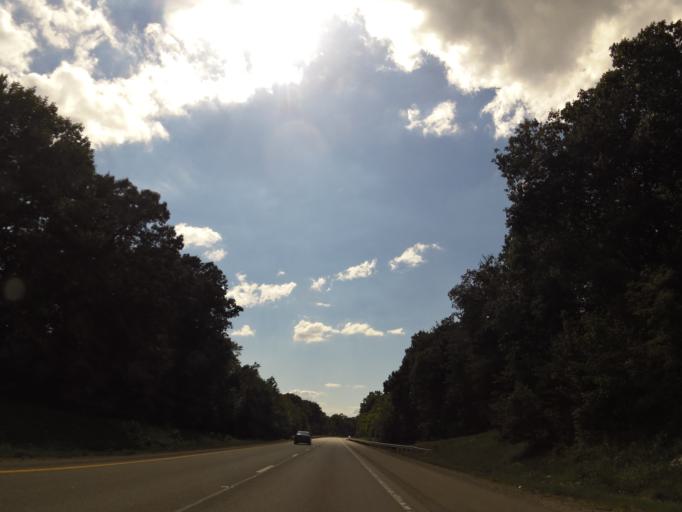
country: US
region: Tennessee
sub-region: Putnam County
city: Cookeville
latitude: 36.1359
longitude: -85.5523
